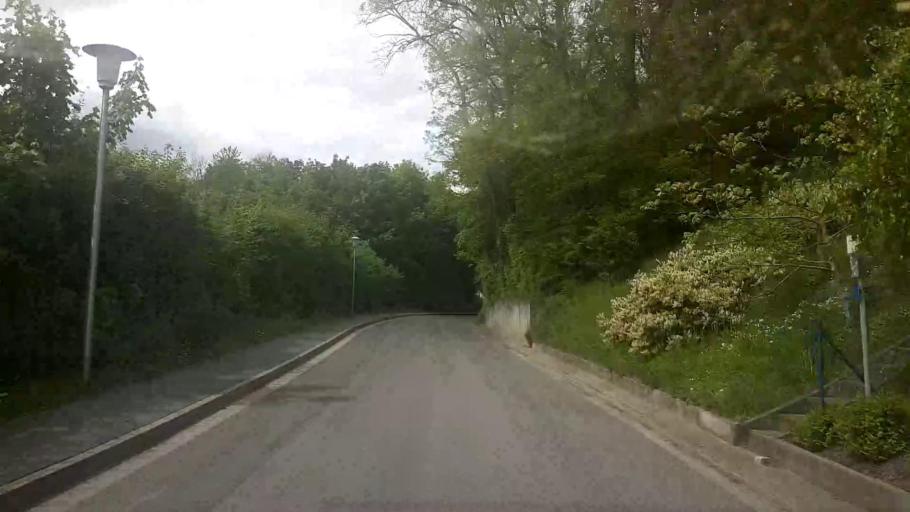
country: DE
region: Bavaria
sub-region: Upper Franconia
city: Untersiemau
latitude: 50.2006
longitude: 10.9880
